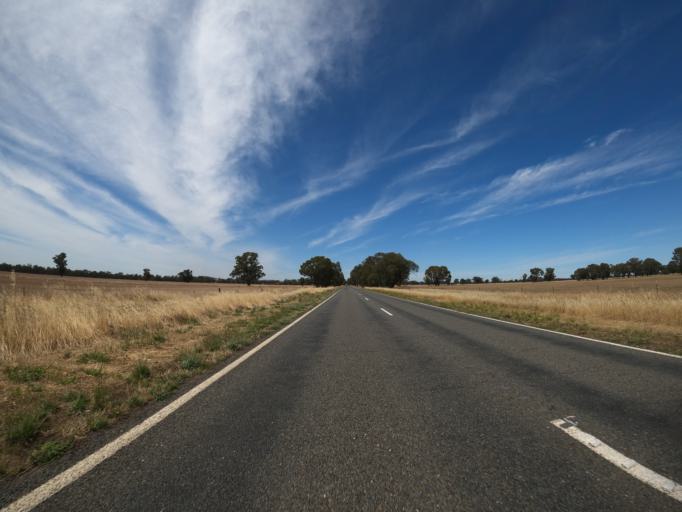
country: AU
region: Victoria
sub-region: Moira
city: Yarrawonga
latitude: -36.2822
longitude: 145.9523
